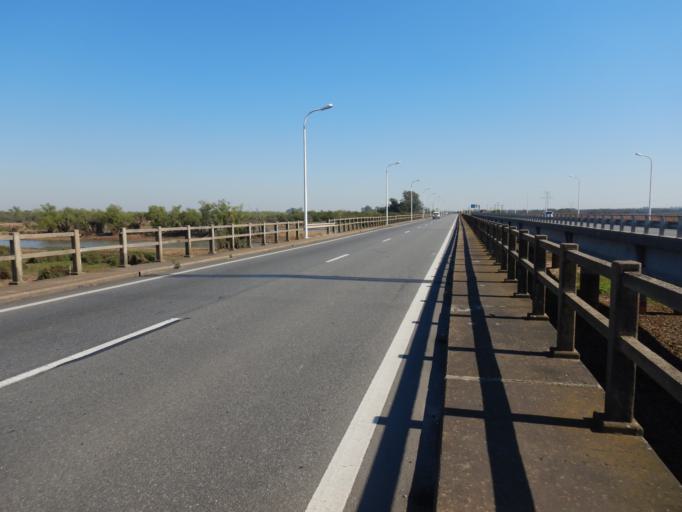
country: AR
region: Entre Rios
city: Parana
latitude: -31.6734
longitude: -60.5774
